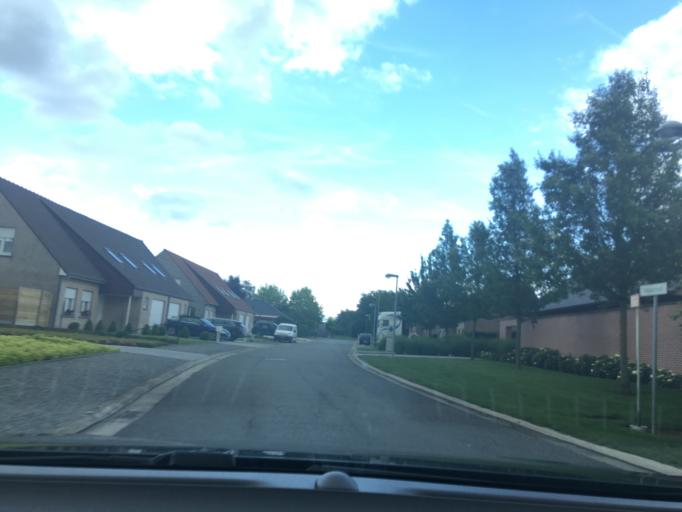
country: BE
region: Flanders
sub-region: Provincie West-Vlaanderen
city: Moorslede
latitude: 50.9372
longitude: 3.0648
